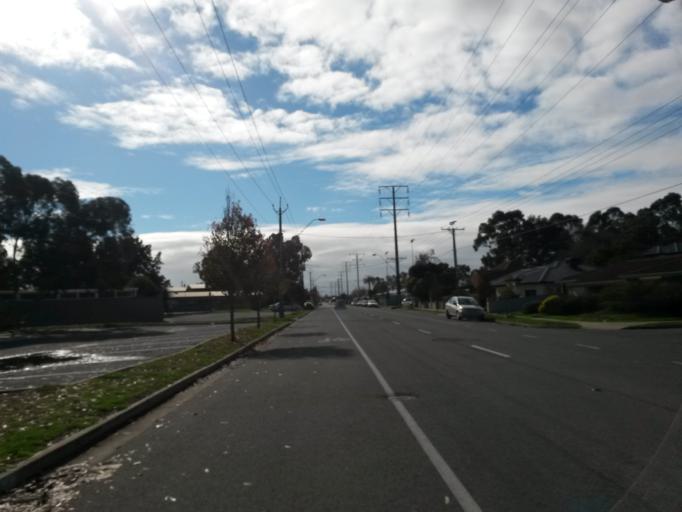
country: AU
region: South Australia
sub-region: Charles Sturt
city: West Lakes Shore
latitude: -34.8477
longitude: 138.4858
